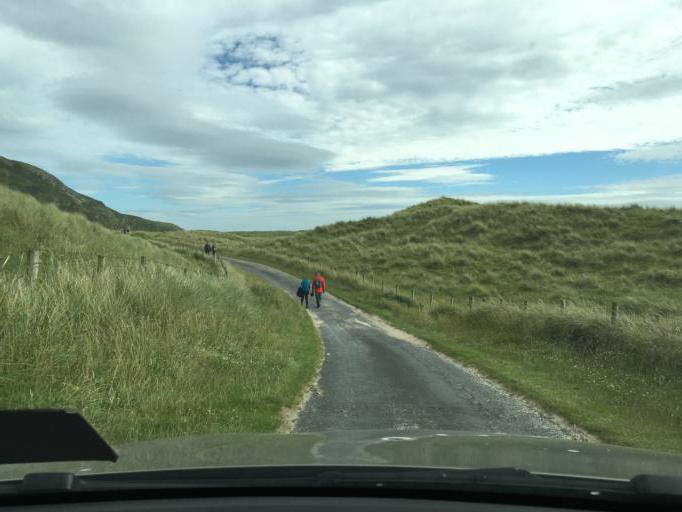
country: IE
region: Ulster
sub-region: County Donegal
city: Carndonagh
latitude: 55.3228
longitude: -7.3286
